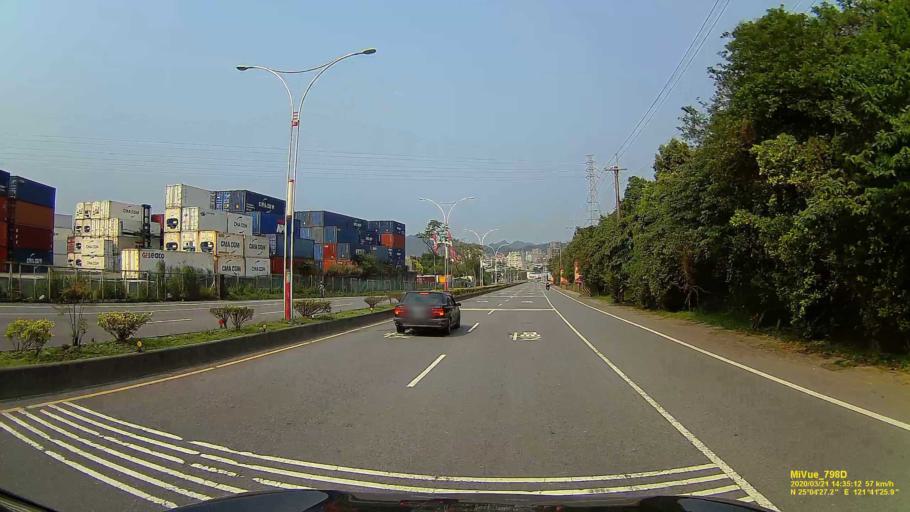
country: TW
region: Taiwan
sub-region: Keelung
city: Keelung
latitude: 25.0746
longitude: 121.6907
